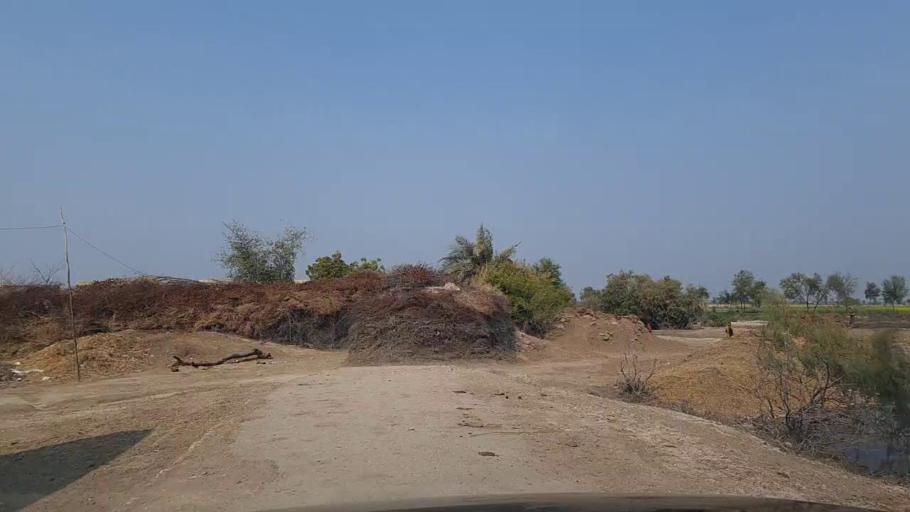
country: PK
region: Sindh
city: Daur
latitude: 26.3864
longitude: 68.3972
